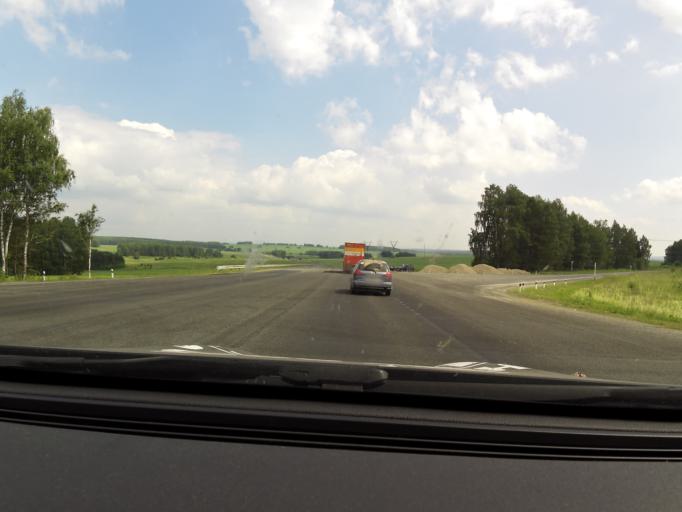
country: RU
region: Sverdlovsk
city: Ufimskiy
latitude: 56.7758
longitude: 57.9949
